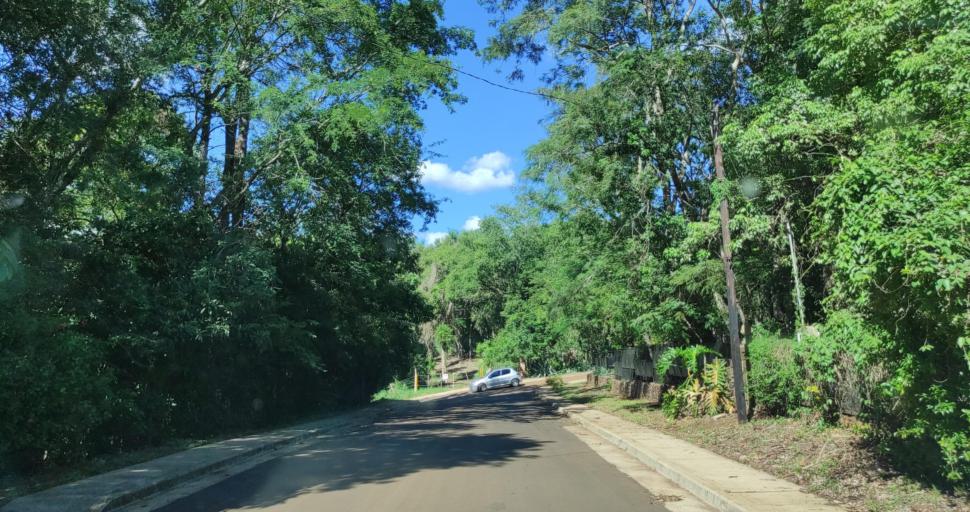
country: AR
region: Misiones
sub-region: Departamento de Candelaria
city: Candelaria
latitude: -27.4497
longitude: -55.7415
